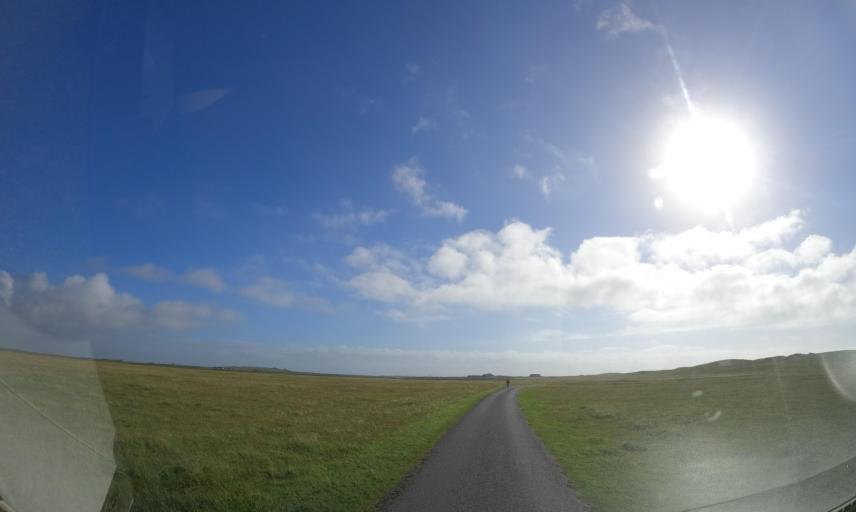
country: GB
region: Scotland
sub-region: Eilean Siar
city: Barra
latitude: 56.4945
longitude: -6.8568
